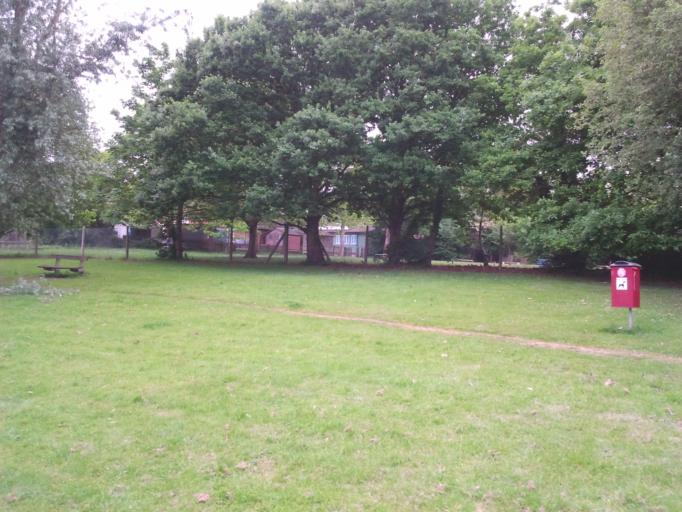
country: GB
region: England
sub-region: Surrey
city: Bagshot
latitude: 51.3588
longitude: -0.6919
